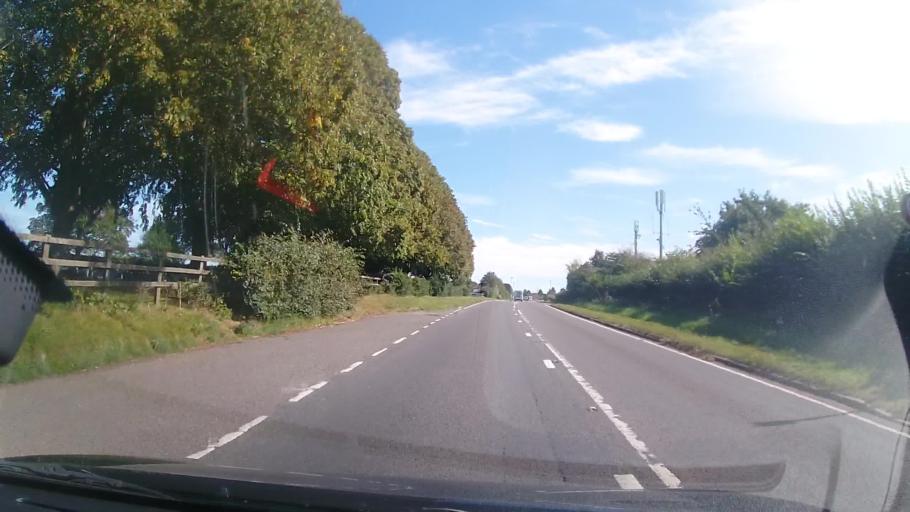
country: GB
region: England
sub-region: Leicestershire
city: Desford
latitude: 52.6276
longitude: -1.3069
